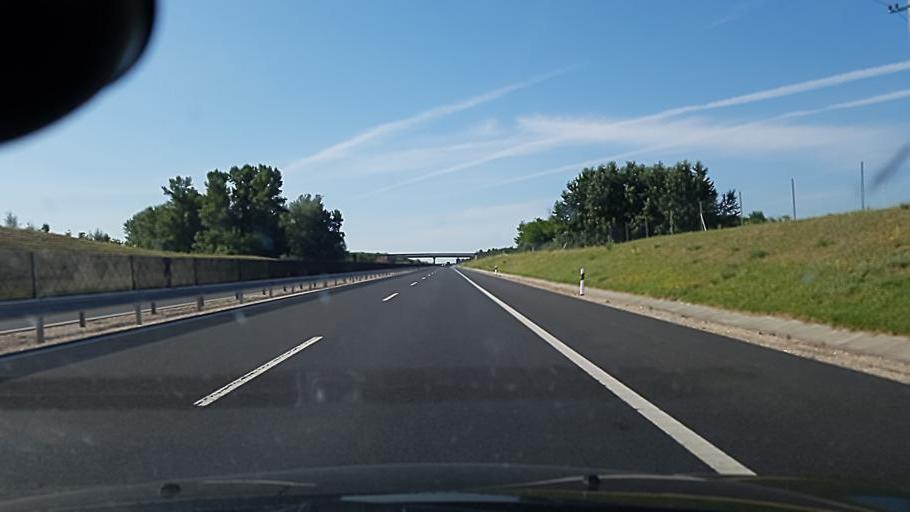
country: HU
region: Tolna
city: Paks
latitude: 46.6208
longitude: 18.8224
